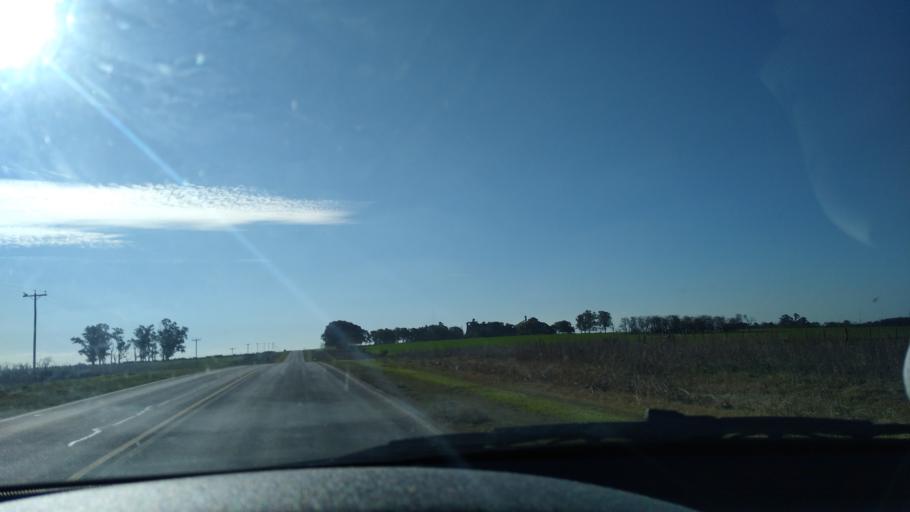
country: AR
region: Entre Rios
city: Aranguren
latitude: -32.3937
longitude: -60.3299
